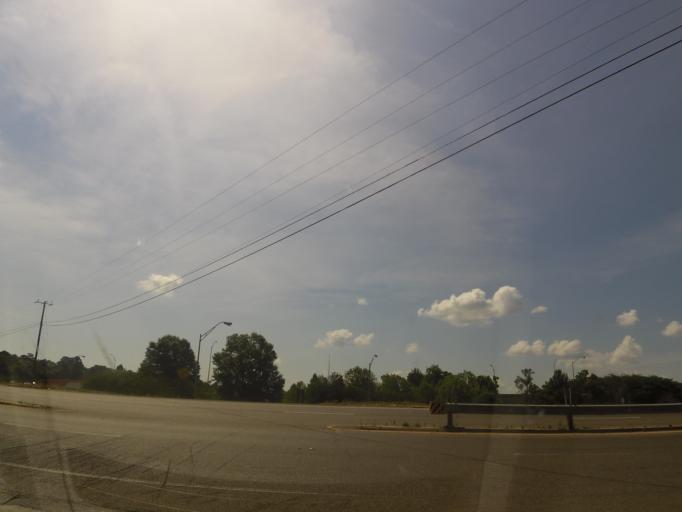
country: US
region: Mississippi
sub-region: Lauderdale County
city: Meridian
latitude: 32.3685
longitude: -88.6735
